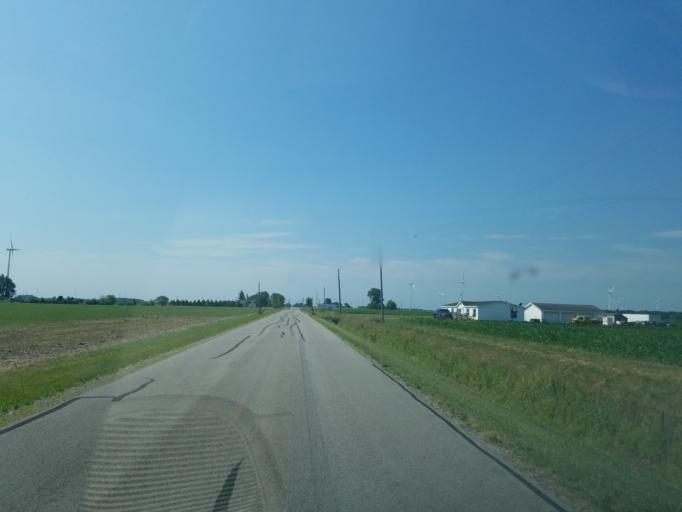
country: US
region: Ohio
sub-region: Van Wert County
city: Convoy
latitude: 40.9503
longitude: -84.6299
